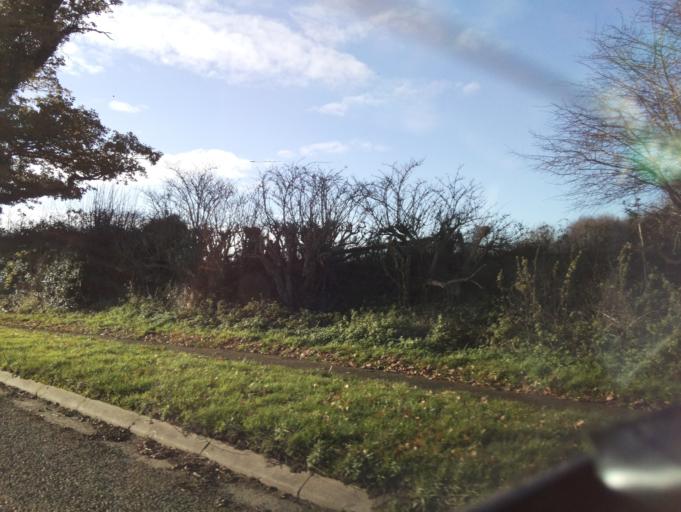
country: GB
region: England
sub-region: Derbyshire
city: Etwall
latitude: 52.8888
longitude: -1.5951
